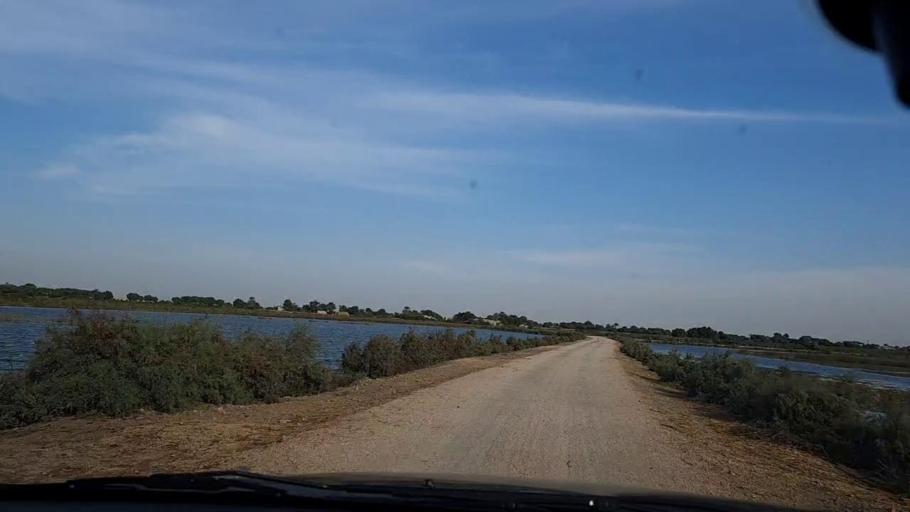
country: PK
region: Sindh
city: Mirpur Batoro
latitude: 24.6545
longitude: 68.2907
